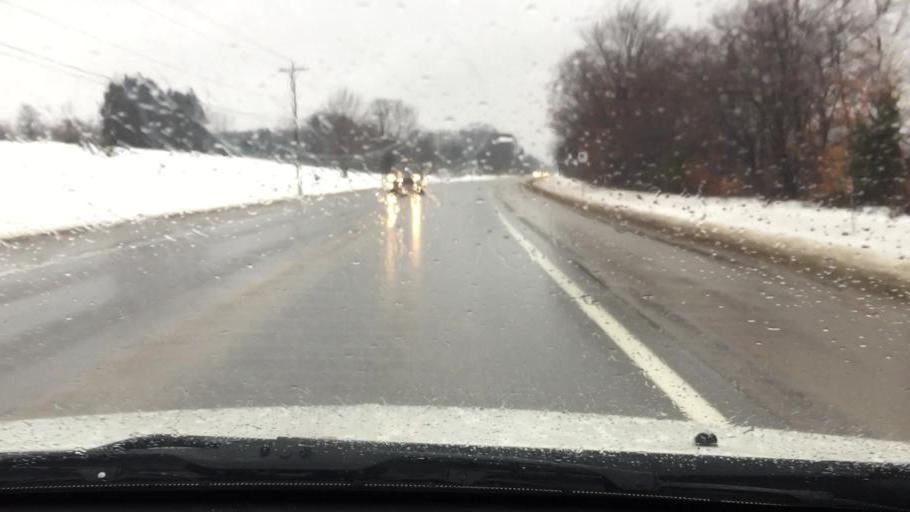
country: US
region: Michigan
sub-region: Charlevoix County
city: Charlevoix
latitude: 45.2834
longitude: -85.2396
